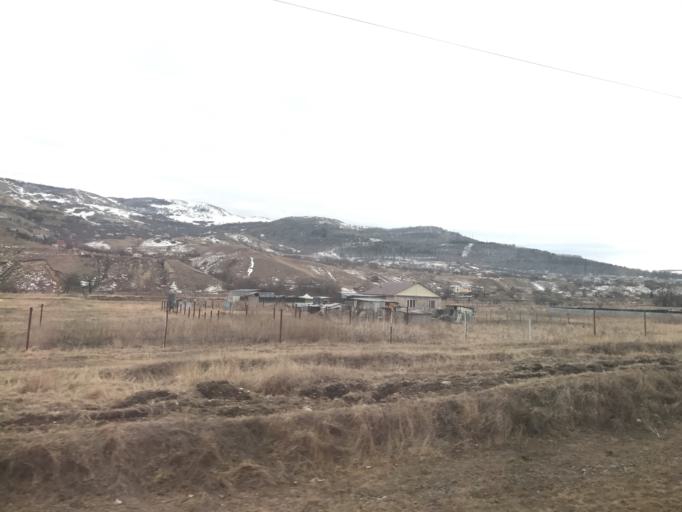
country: RU
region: Stavropol'skiy
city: Kislovodsk
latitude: 43.9513
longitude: 42.7510
